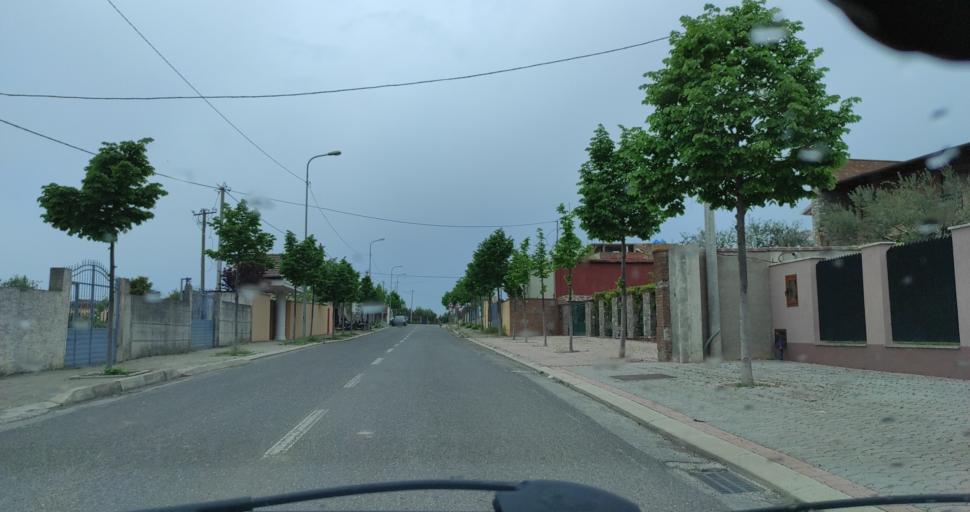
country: AL
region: Lezhe
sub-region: Rrethi i Kurbinit
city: Mamurras
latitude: 41.5860
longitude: 19.6930
